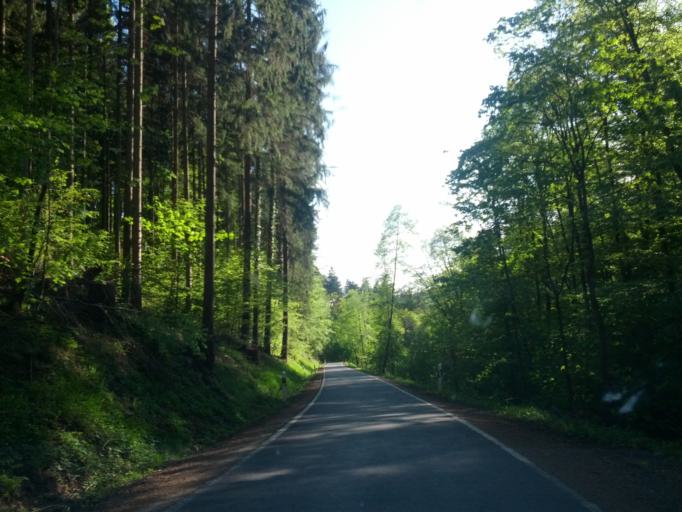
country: DE
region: Thuringia
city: Geismar
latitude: 51.2079
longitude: 10.1722
